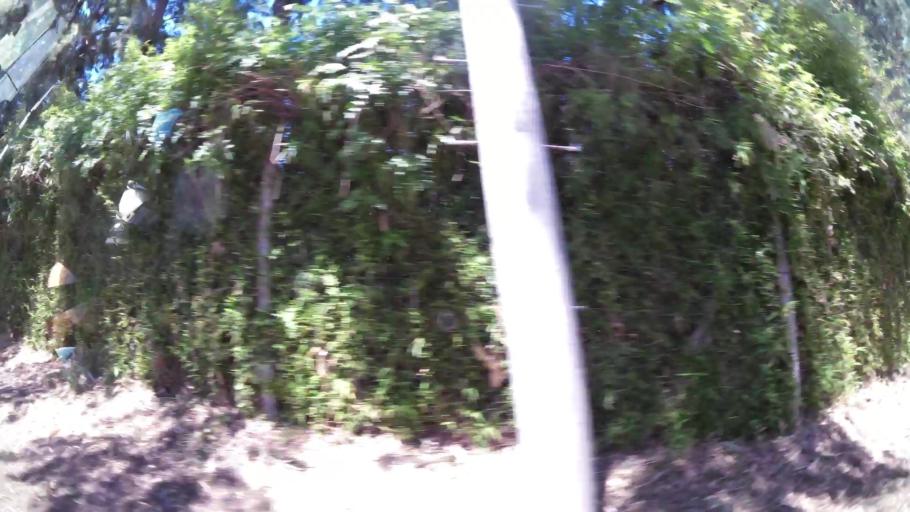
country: AR
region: Buenos Aires
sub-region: Partido de Tigre
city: Tigre
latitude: -34.4430
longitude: -58.5408
